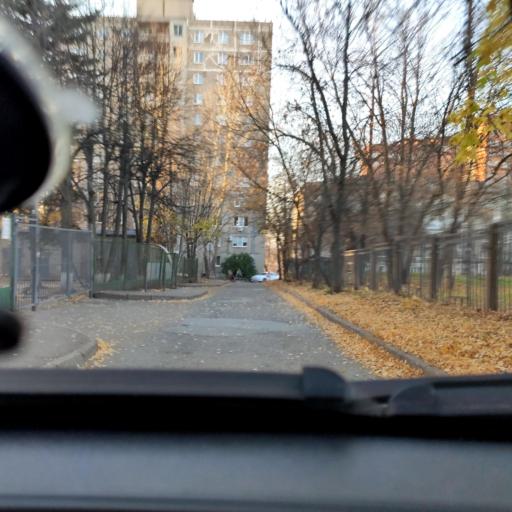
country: RU
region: Bashkortostan
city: Ufa
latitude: 54.7617
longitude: 55.9924
